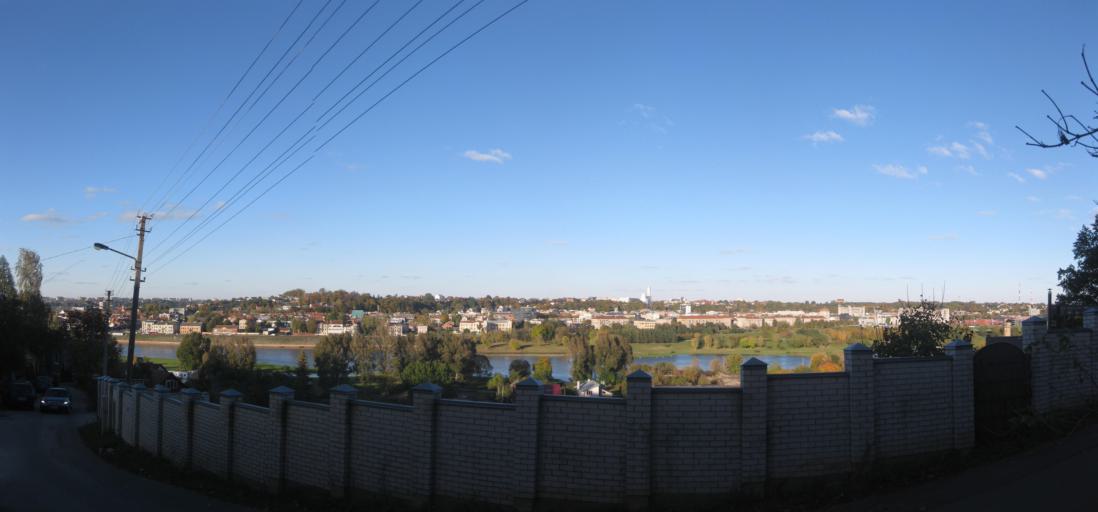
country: LT
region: Kauno apskritis
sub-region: Kaunas
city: Aleksotas
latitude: 54.8890
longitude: 23.8983
